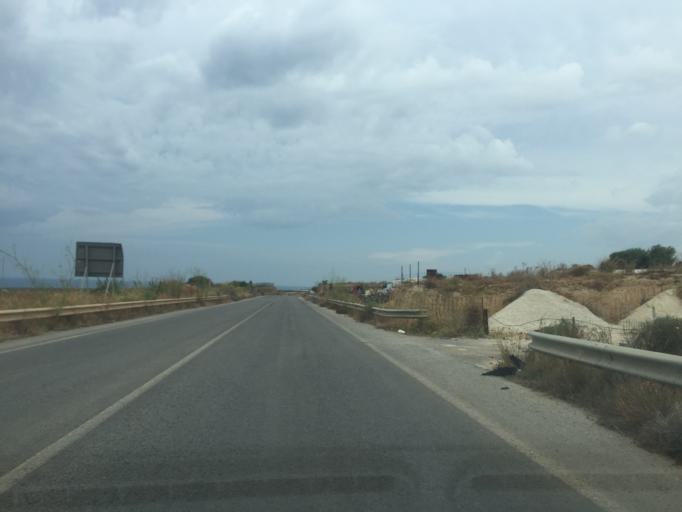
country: IT
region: Sicily
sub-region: Ragusa
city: Donnalucata
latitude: 36.7725
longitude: 14.6253
